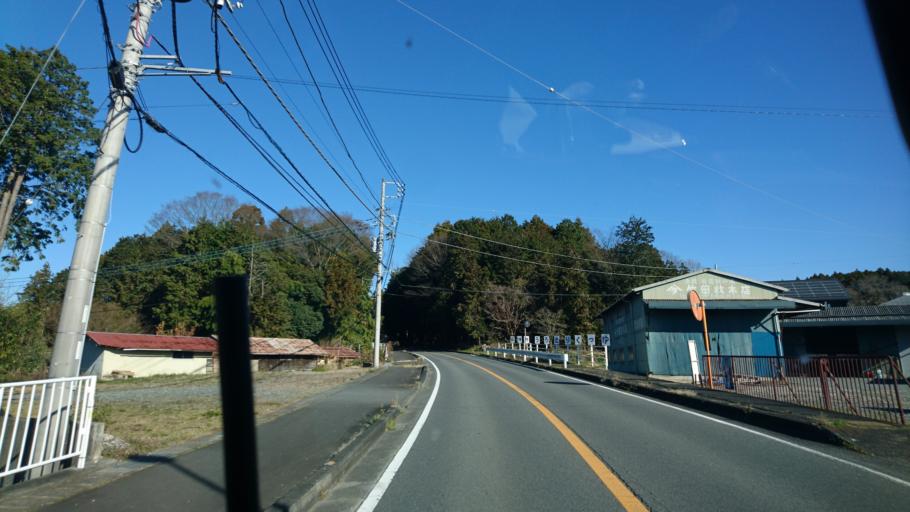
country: JP
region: Shizuoka
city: Fujinomiya
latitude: 35.2625
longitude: 138.6060
